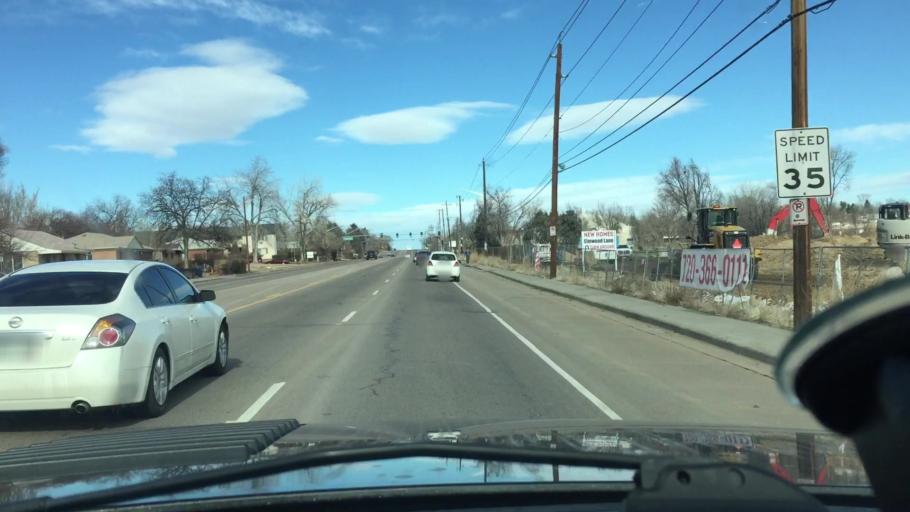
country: US
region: Colorado
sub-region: Adams County
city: Sherrelwood
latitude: 39.8399
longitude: -105.0060
